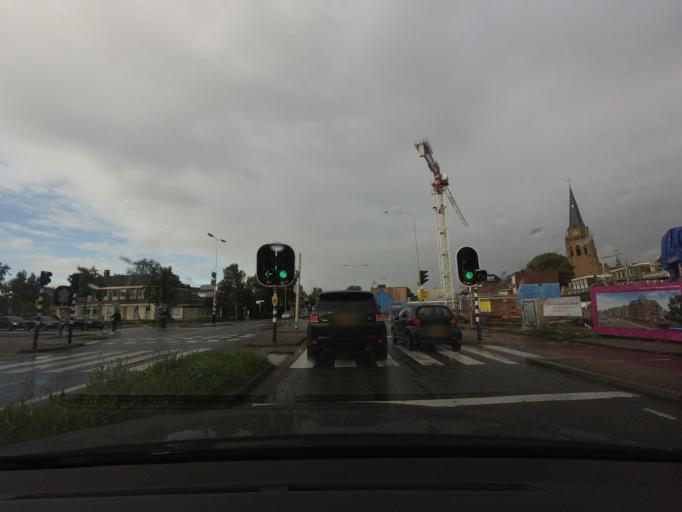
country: NL
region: South Holland
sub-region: Gemeente Voorschoten
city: Voorschoten
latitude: 52.1245
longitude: 4.4445
